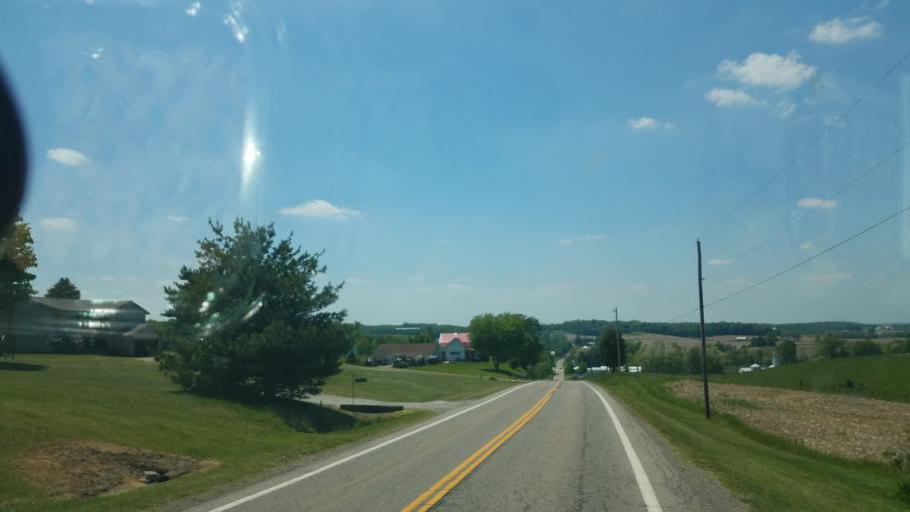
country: US
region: Ohio
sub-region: Knox County
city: Oak Hill
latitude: 40.2855
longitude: -82.2691
